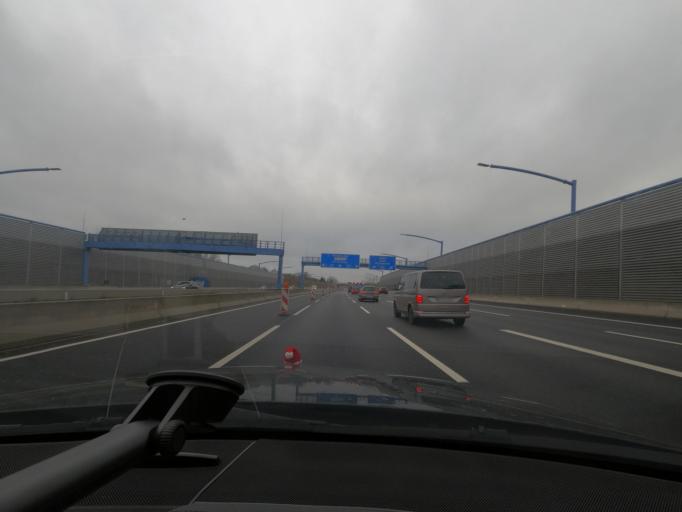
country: DE
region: Hamburg
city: Eidelstedt
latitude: 53.5990
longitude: 9.9134
